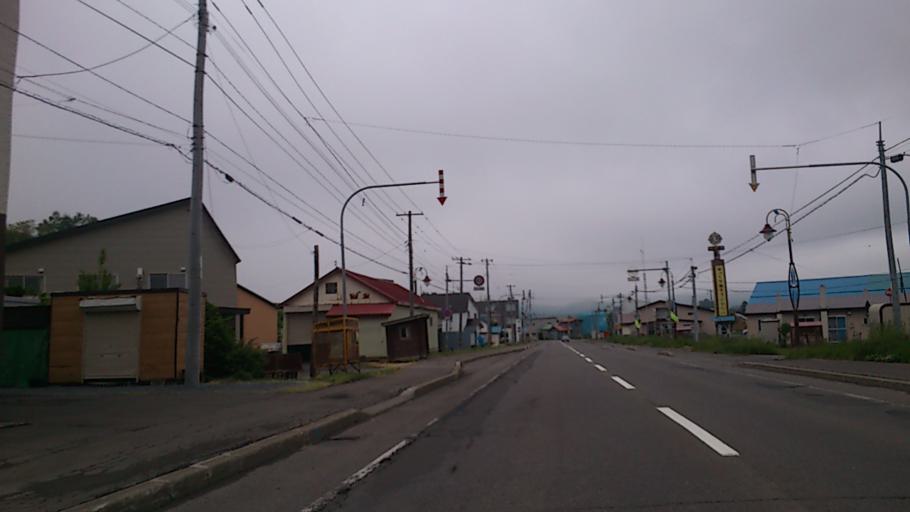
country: JP
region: Hokkaido
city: Niseko Town
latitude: 42.8550
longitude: 140.8906
